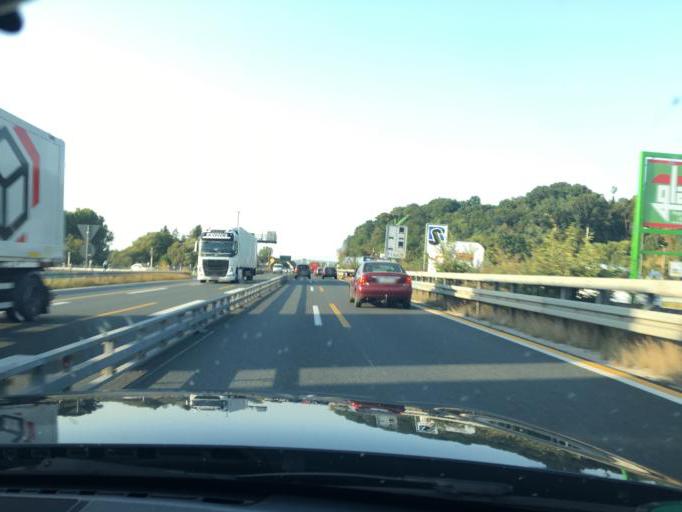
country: DE
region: Bavaria
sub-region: Regierungsbezirk Mittelfranken
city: Erlangen
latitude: 49.6062
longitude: 10.9984
